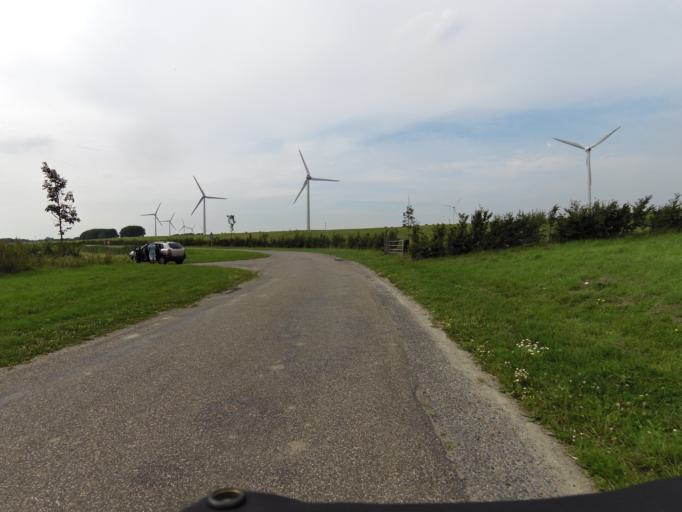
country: NL
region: South Holland
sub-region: Gemeente Spijkenisse
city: Spijkenisse
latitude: 51.8630
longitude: 4.2808
